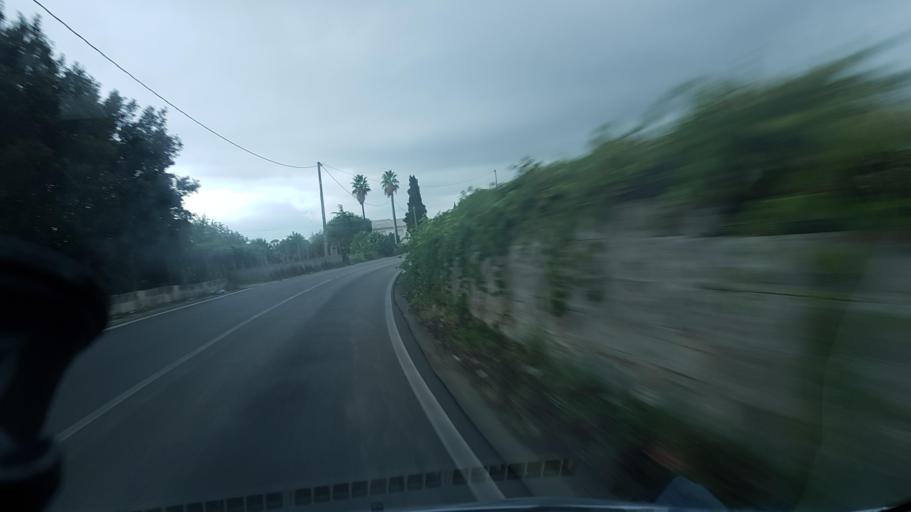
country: IT
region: Apulia
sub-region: Provincia di Lecce
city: Novoli
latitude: 40.3639
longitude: 18.0666
